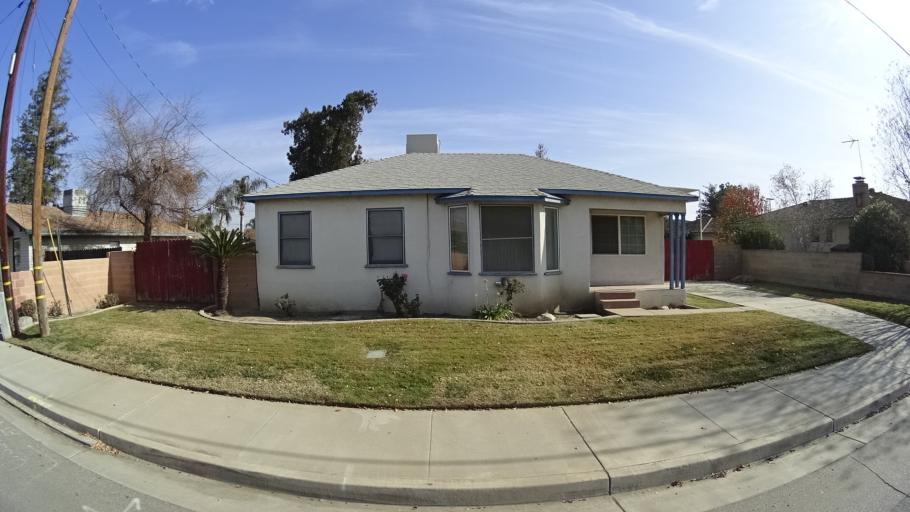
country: US
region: California
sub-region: Kern County
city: Greenacres
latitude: 35.3814
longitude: -119.1098
